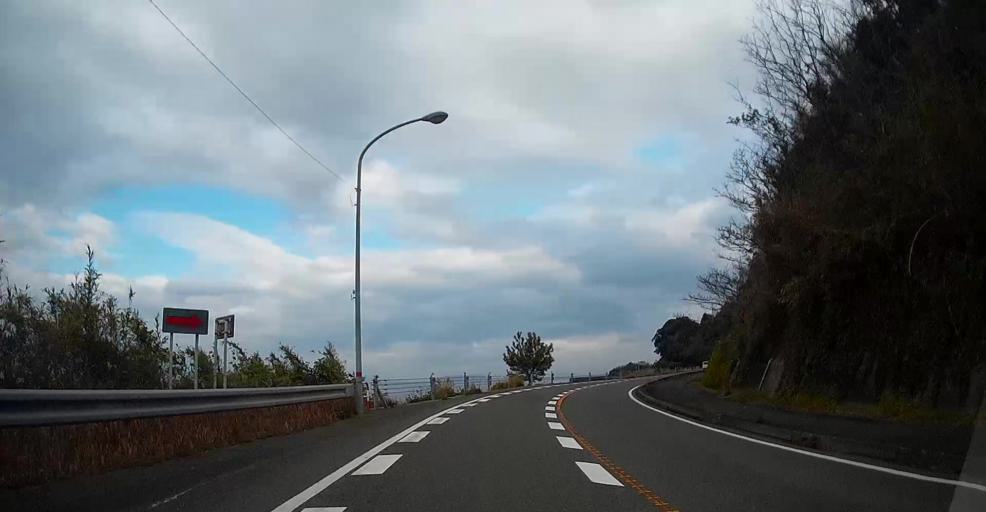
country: JP
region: Kumamoto
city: Hondo
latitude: 32.5008
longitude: 130.2987
